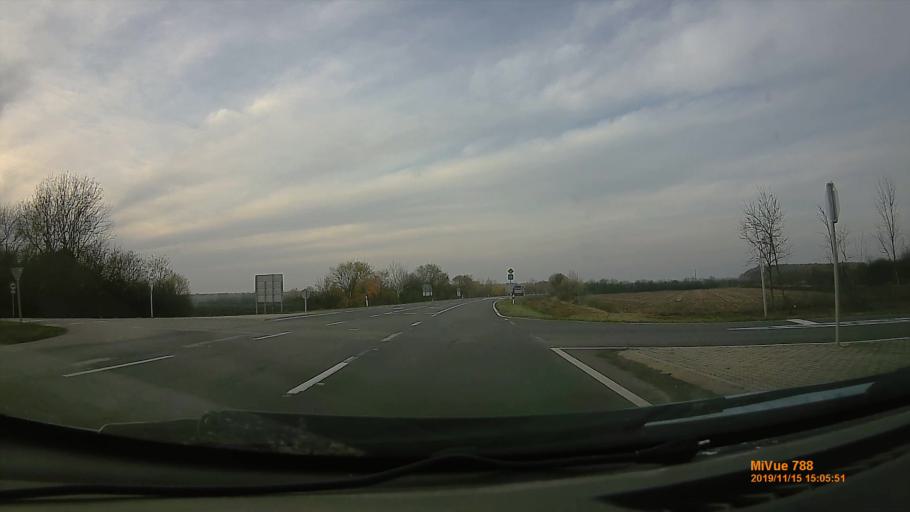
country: HU
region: Bekes
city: Gyula
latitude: 46.6373
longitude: 21.2503
